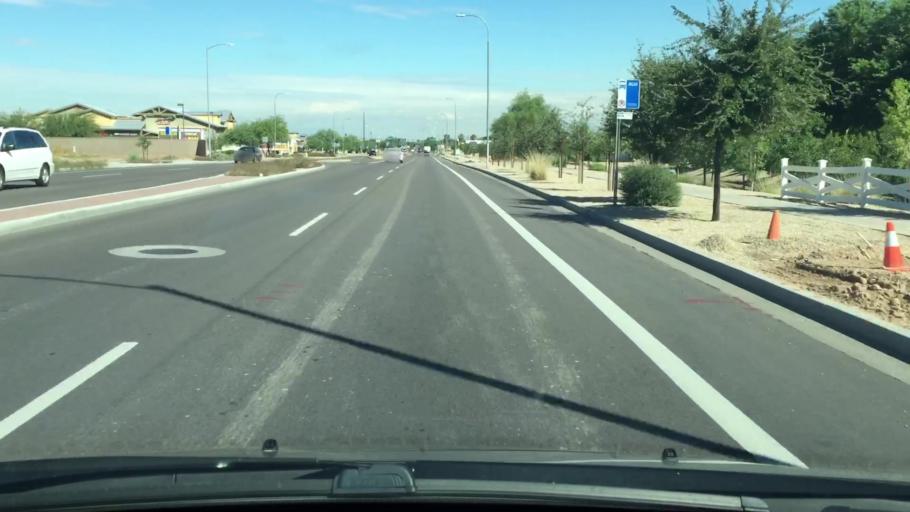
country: US
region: Arizona
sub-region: Maricopa County
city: Laveen
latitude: 33.3876
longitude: -112.1336
